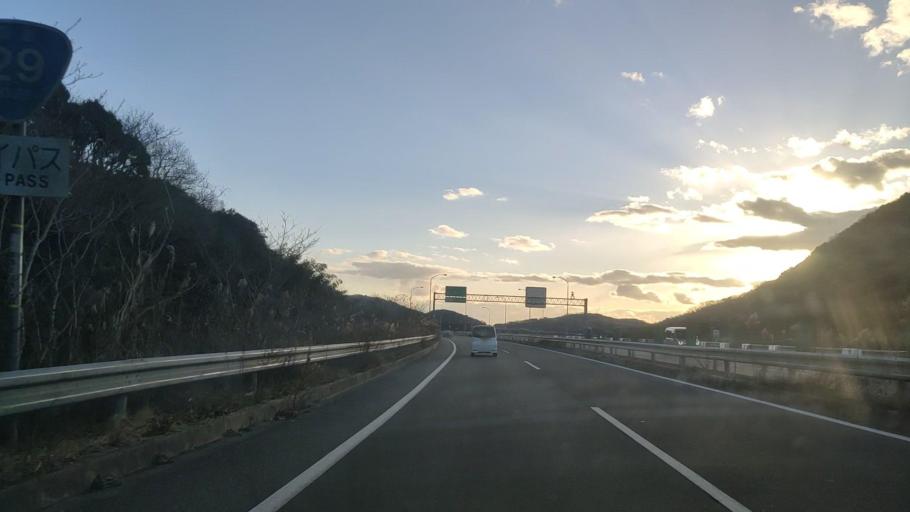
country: JP
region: Hyogo
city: Tatsunocho-tominaga
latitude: 34.8544
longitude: 134.6064
